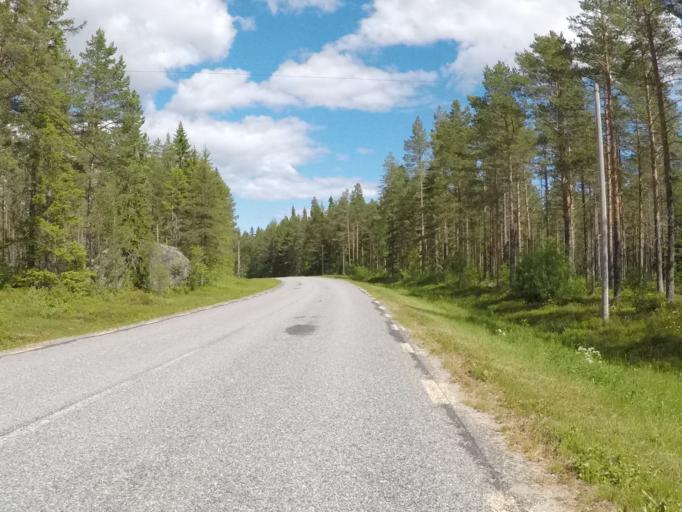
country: SE
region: Vaesterbotten
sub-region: Robertsfors Kommun
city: Robertsfors
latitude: 63.9582
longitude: 20.8055
